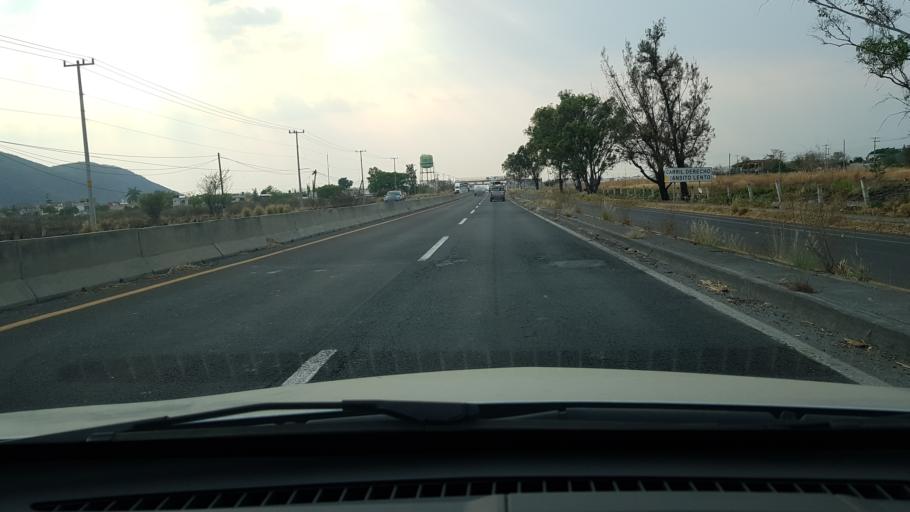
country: MX
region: Morelos
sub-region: Ayala
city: Unidad Habitacional Mariano Matamoros
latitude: 18.7489
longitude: -98.8476
